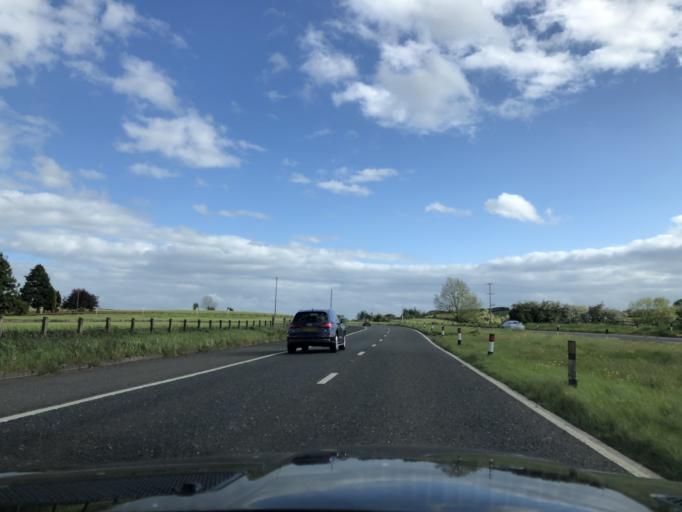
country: GB
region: Northern Ireland
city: Cullybackey
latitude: 54.9322
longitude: -6.3274
